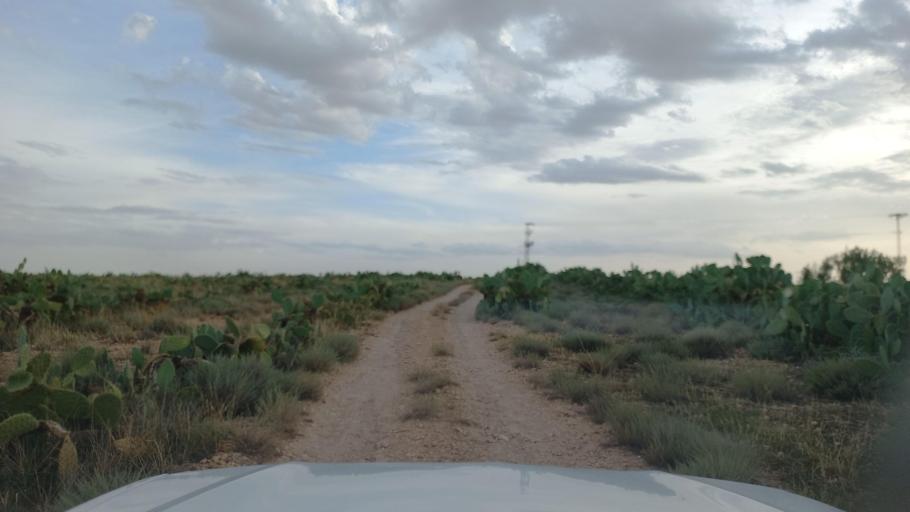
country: TN
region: Al Qasrayn
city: Sbiba
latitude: 35.4409
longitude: 9.0877
